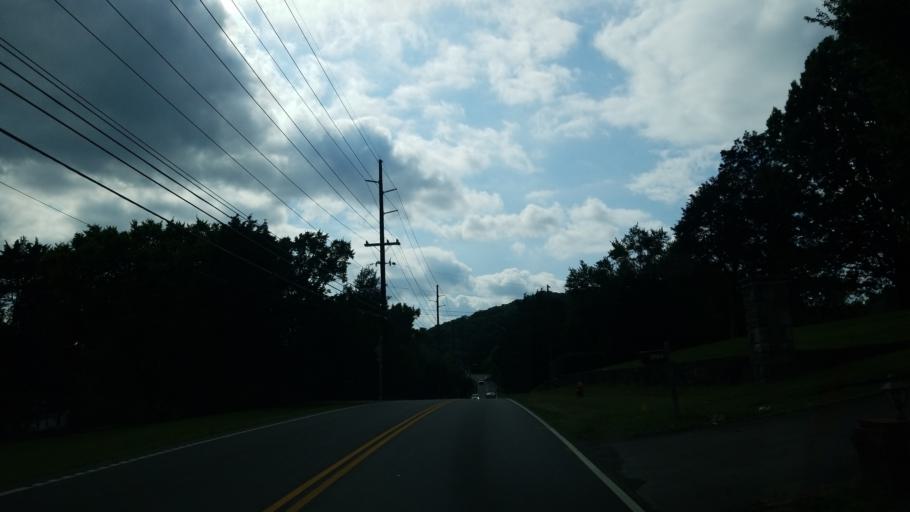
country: US
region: Tennessee
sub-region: Davidson County
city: Forest Hills
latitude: 36.0435
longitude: -86.8440
